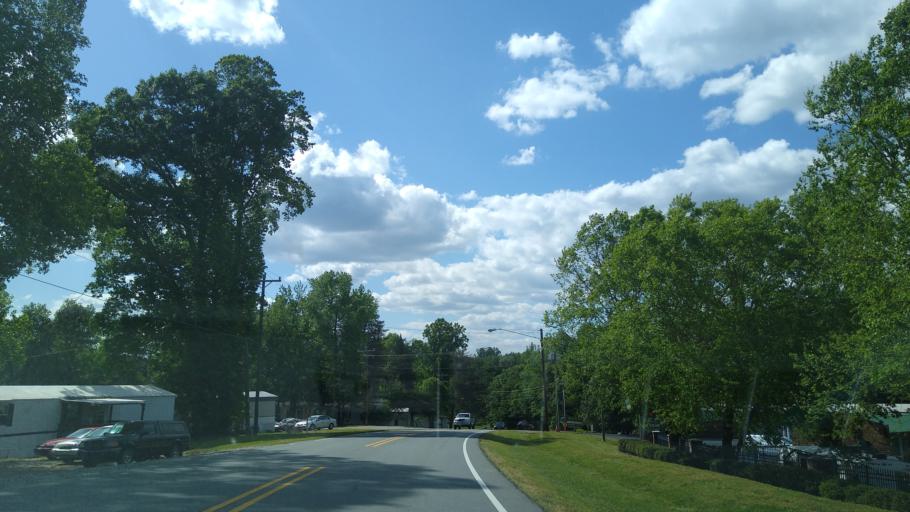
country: US
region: North Carolina
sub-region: Forsyth County
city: Kernersville
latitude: 36.0945
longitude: -80.0672
